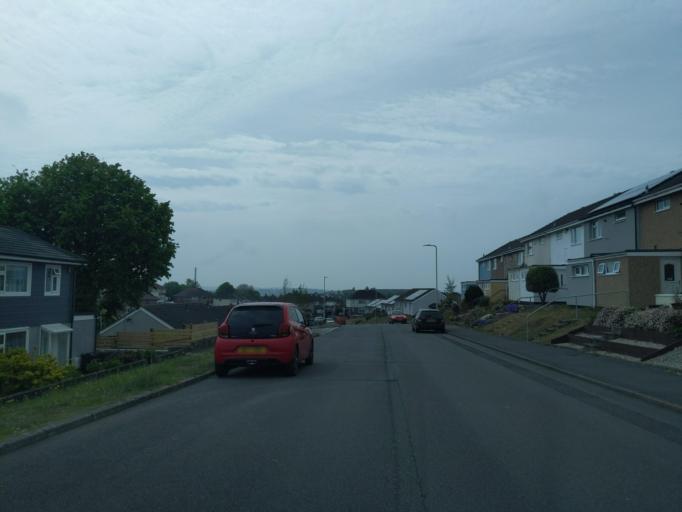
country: GB
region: England
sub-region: Cornwall
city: Torpoint
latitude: 50.4037
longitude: -4.1755
